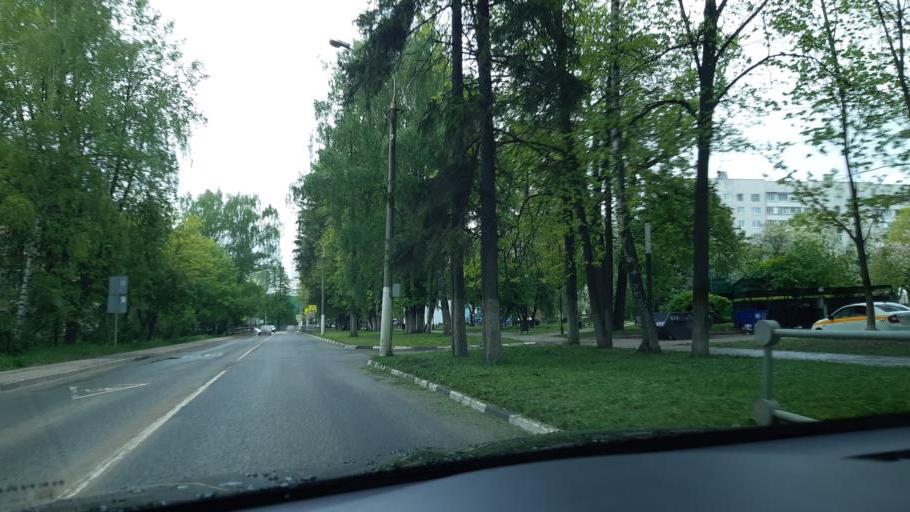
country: RU
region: Moskovskaya
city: Dolgoprudnyy
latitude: 55.9513
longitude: 37.4913
